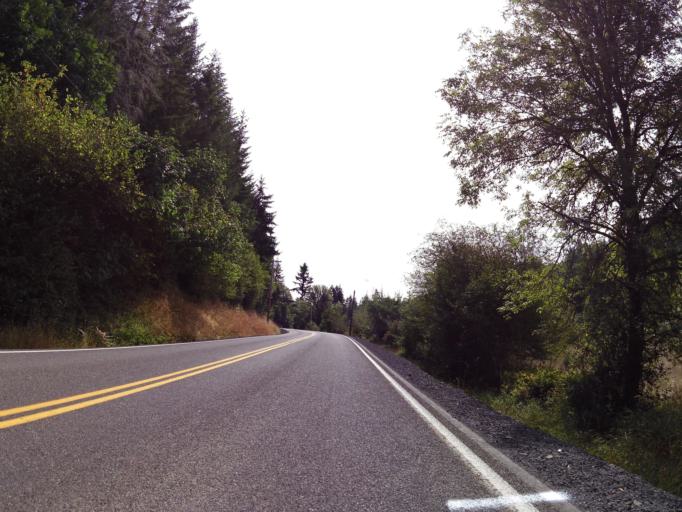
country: US
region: Washington
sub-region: Lewis County
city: Napavine
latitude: 46.5686
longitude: -122.9675
